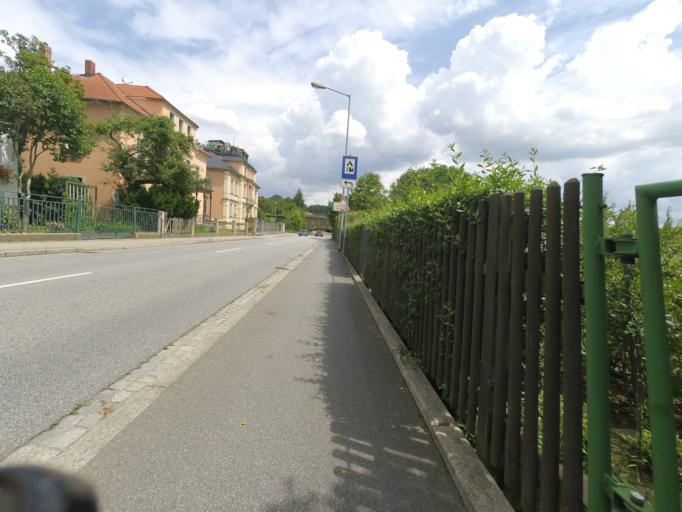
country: DE
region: Saxony
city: Pirna
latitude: 50.9666
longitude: 13.9323
